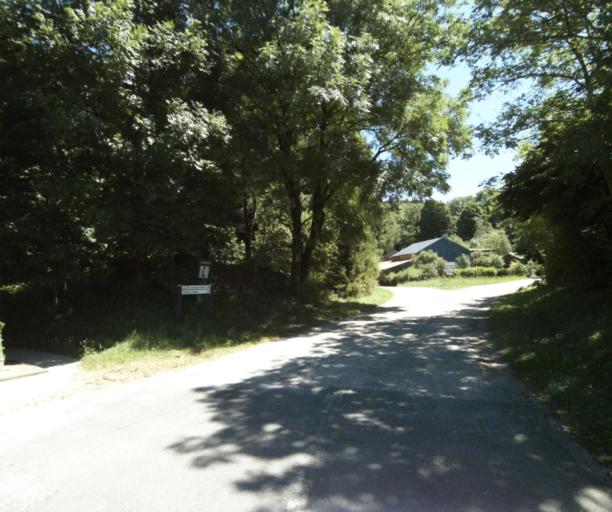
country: FR
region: Midi-Pyrenees
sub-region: Departement du Tarn
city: Dourgne
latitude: 43.4440
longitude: 2.1979
